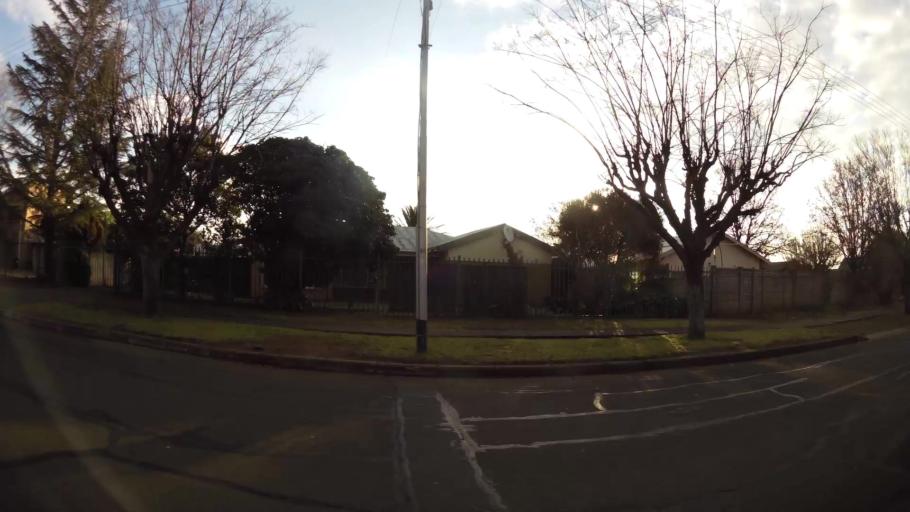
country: ZA
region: Orange Free State
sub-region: Mangaung Metropolitan Municipality
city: Bloemfontein
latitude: -29.1426
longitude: 26.1923
